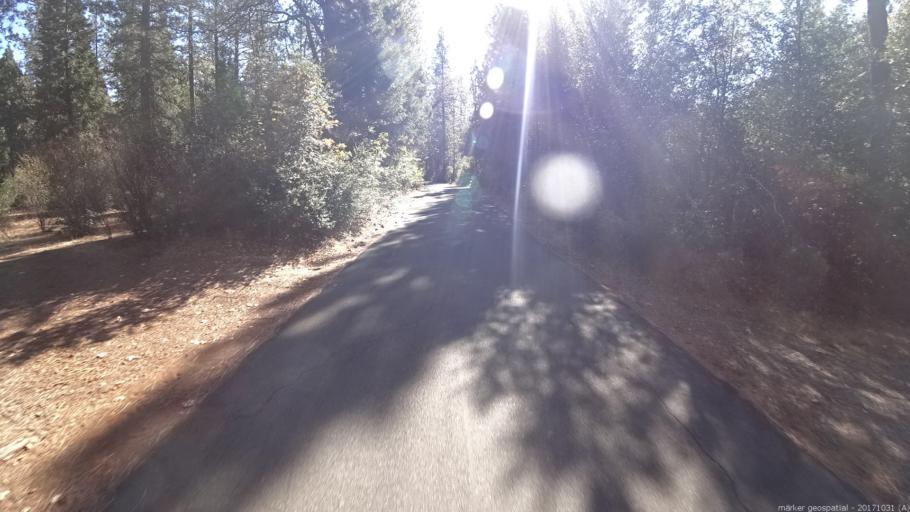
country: US
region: California
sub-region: Shasta County
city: Shingletown
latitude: 40.5317
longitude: -121.9296
